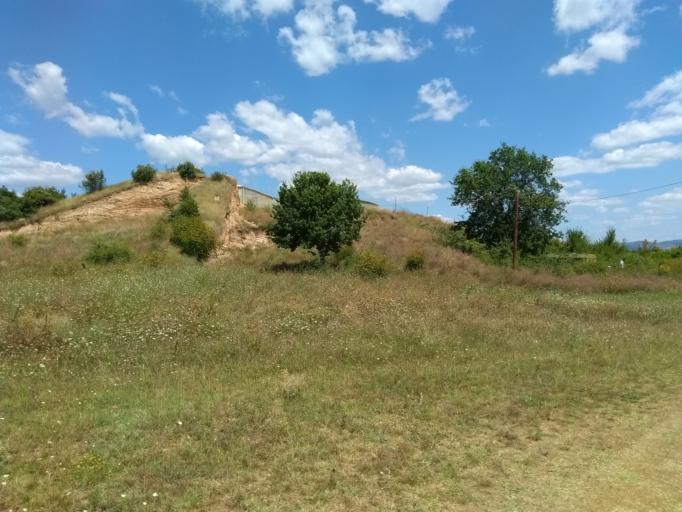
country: BG
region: Sliven
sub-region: Obshtina Nova Zagora
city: Nova Zagora
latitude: 42.5204
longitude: 25.9136
